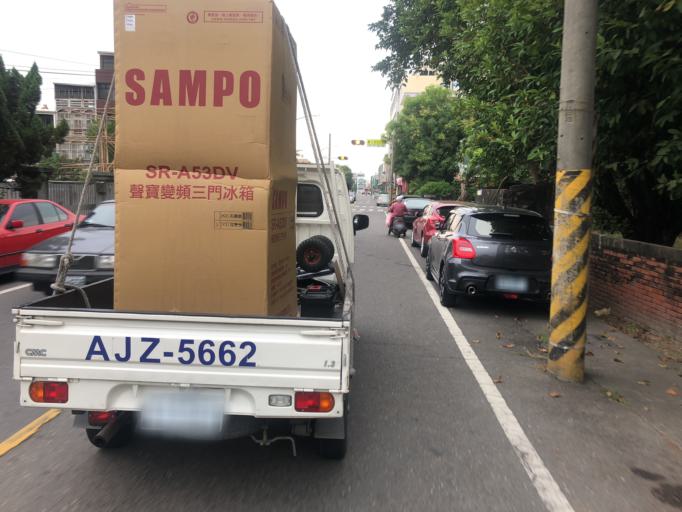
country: TW
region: Taiwan
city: Xinying
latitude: 23.1831
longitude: 120.2452
